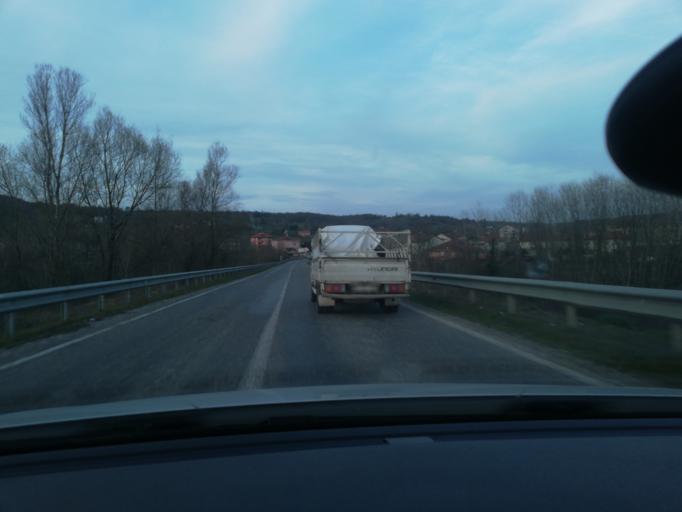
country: TR
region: Zonguldak
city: Saltukova
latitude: 41.5251
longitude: 32.0941
